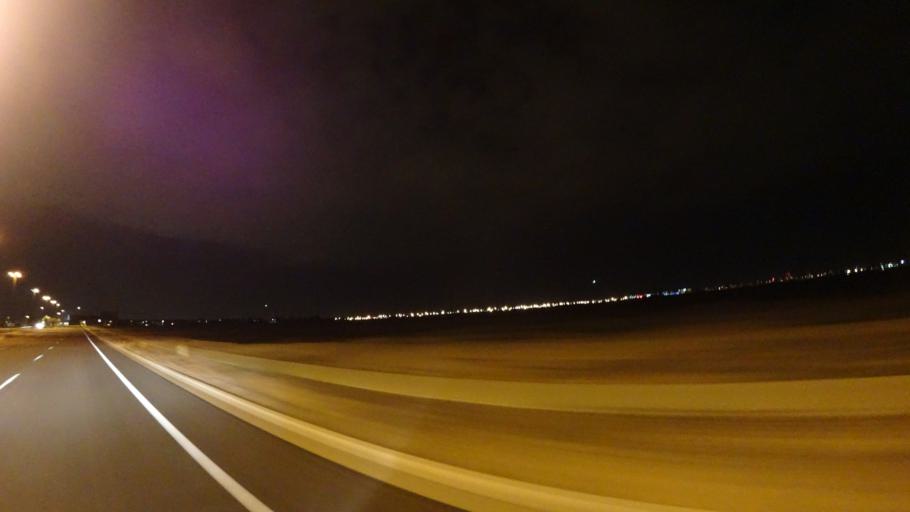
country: US
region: Arizona
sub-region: Maricopa County
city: Queen Creek
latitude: 33.2906
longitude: -111.6960
